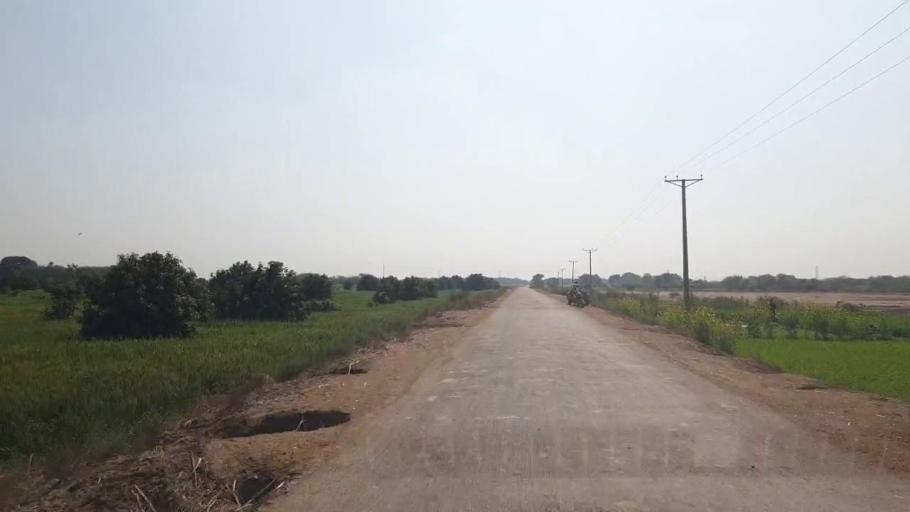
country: PK
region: Sindh
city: Chambar
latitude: 25.3981
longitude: 68.8958
